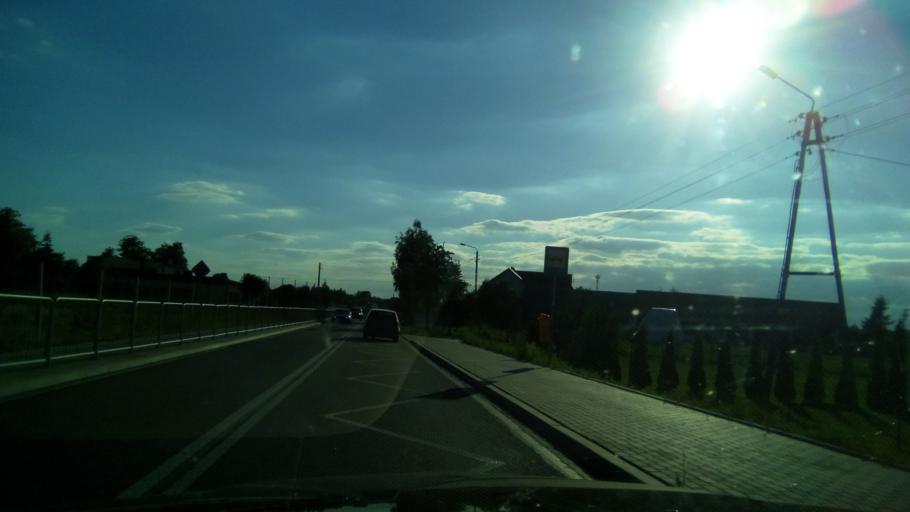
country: PL
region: Masovian Voivodeship
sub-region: Powiat bialobrzeski
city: Stromiec
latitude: 51.6179
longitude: 21.2041
